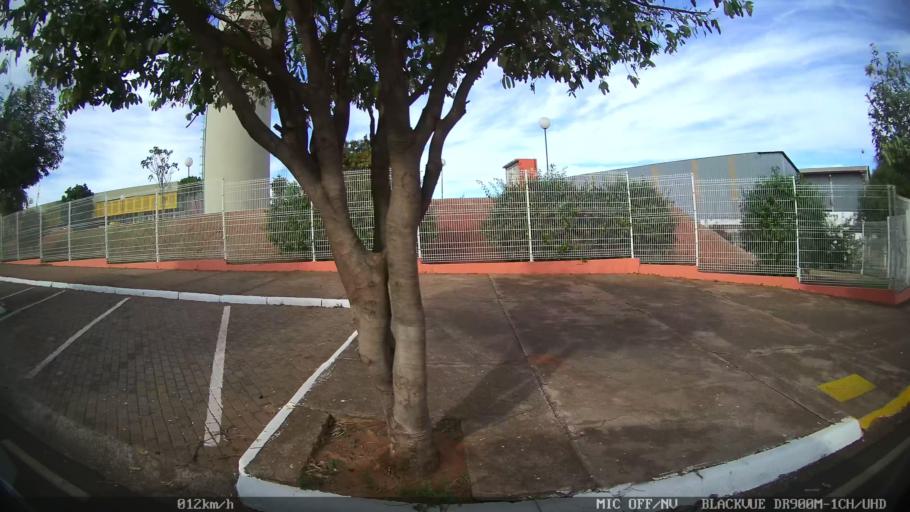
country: BR
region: Sao Paulo
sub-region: Catanduva
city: Catanduva
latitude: -21.1272
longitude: -49.0025
